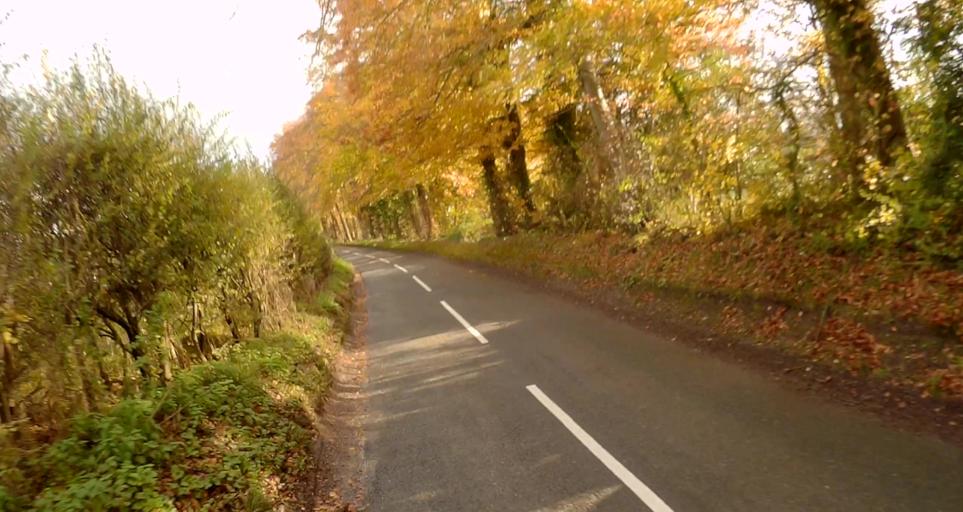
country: GB
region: England
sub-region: Hampshire
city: Old Basing
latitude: 51.2475
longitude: -1.0455
